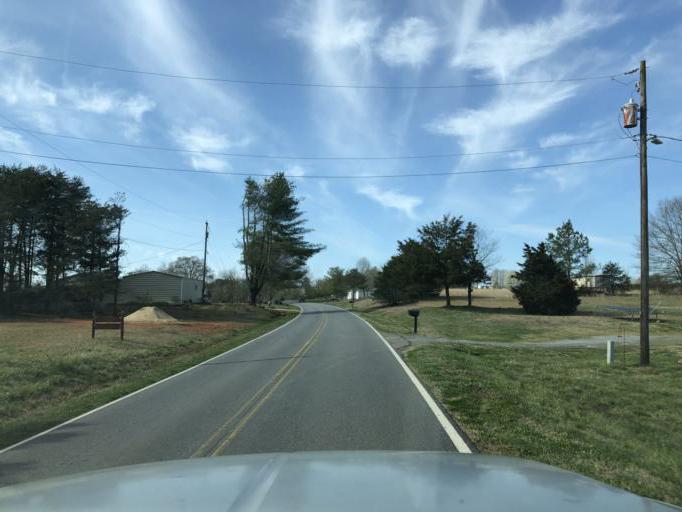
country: US
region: North Carolina
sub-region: Burke County
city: Salem
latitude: 35.5024
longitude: -81.6307
